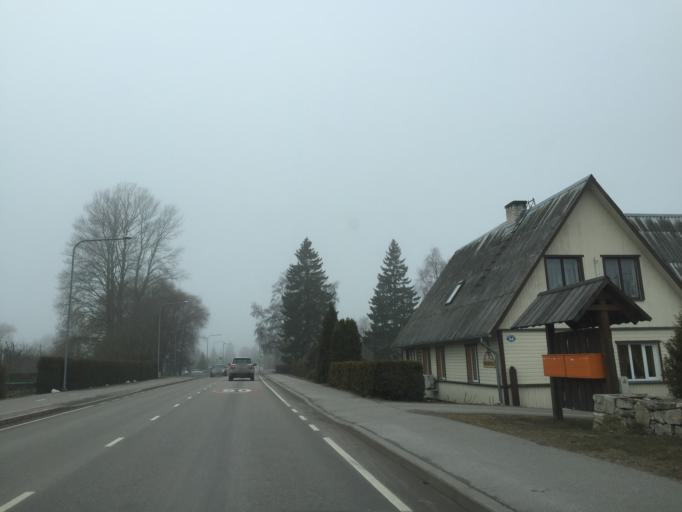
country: EE
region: Saare
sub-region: Kuressaare linn
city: Kuressaare
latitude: 58.2287
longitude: 22.3878
